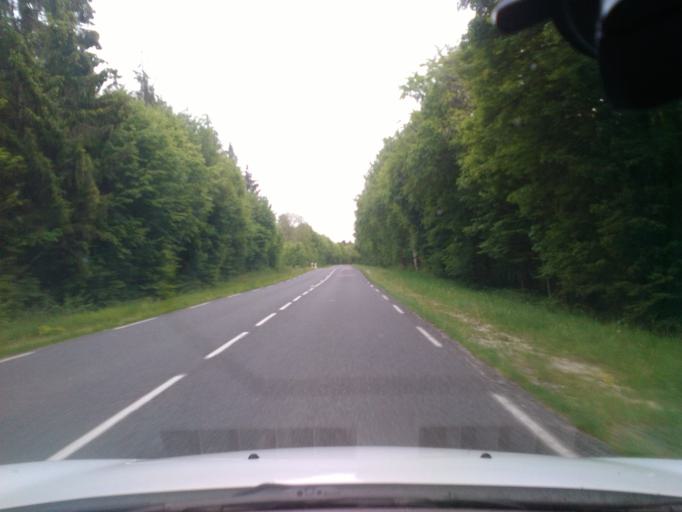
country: FR
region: Champagne-Ardenne
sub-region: Departement de la Haute-Marne
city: Lavilleneuve-au-Roi
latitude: 48.2116
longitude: 4.9218
